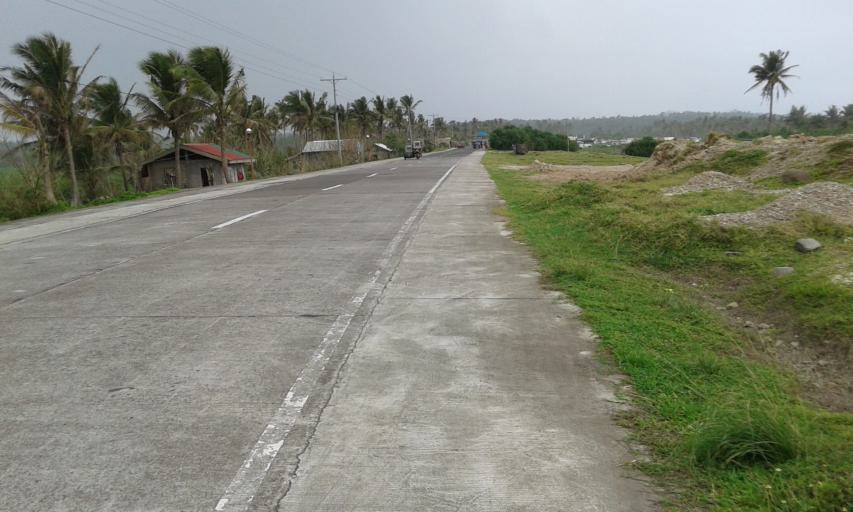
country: PH
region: Bicol
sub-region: Province of Sorsogon
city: Gubat
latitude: 12.9017
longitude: 124.1173
